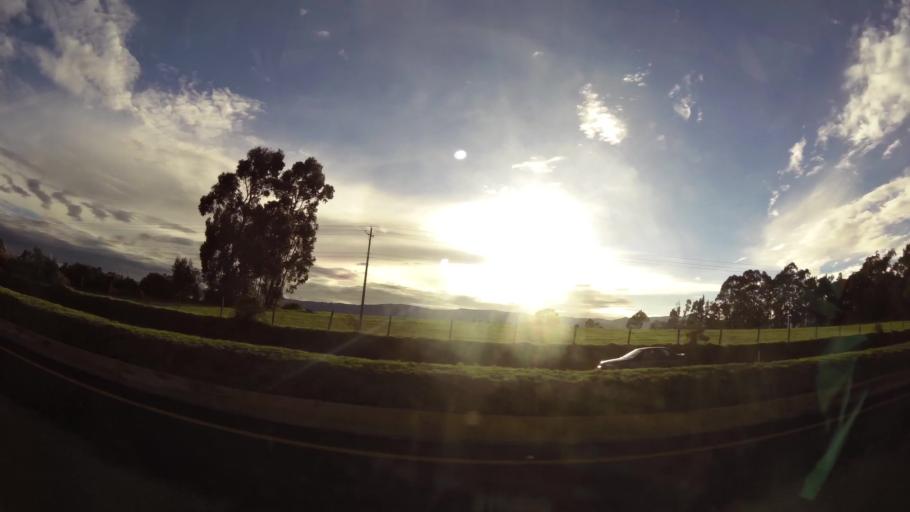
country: EC
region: Cotopaxi
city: Saquisili
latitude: -0.8244
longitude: -78.6216
